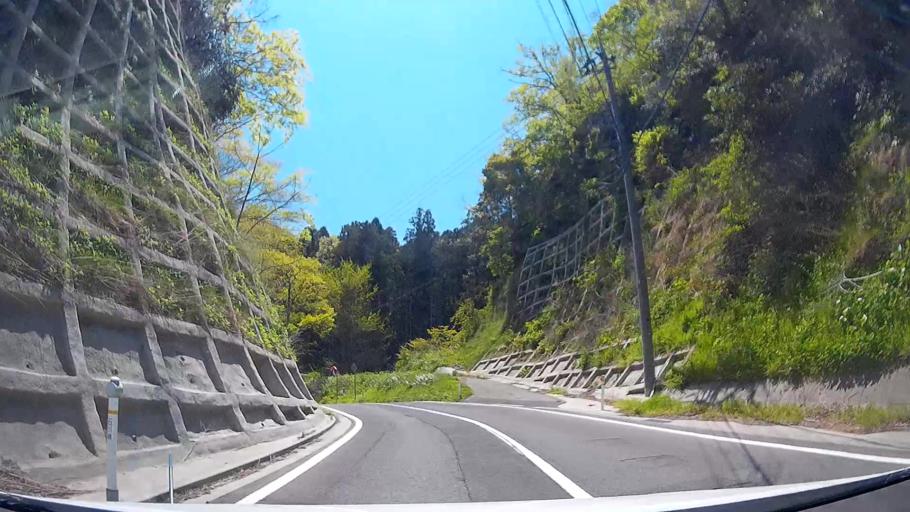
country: JP
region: Ishikawa
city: Nanao
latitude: 37.5247
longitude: 137.2999
